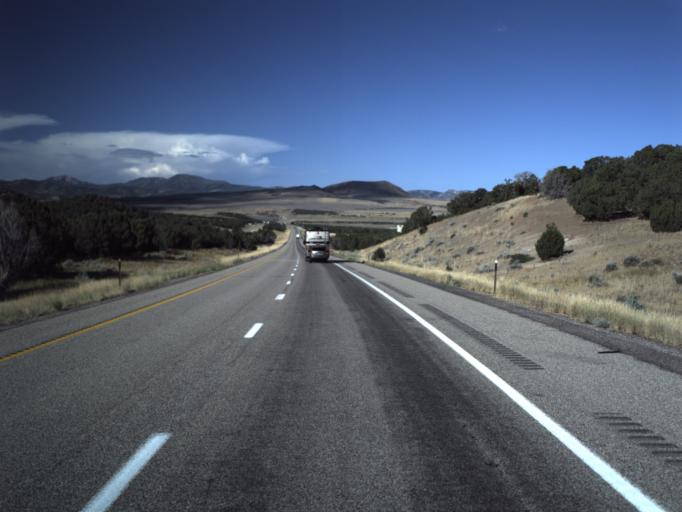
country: US
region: Utah
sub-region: Beaver County
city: Beaver
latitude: 38.6033
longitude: -112.5530
